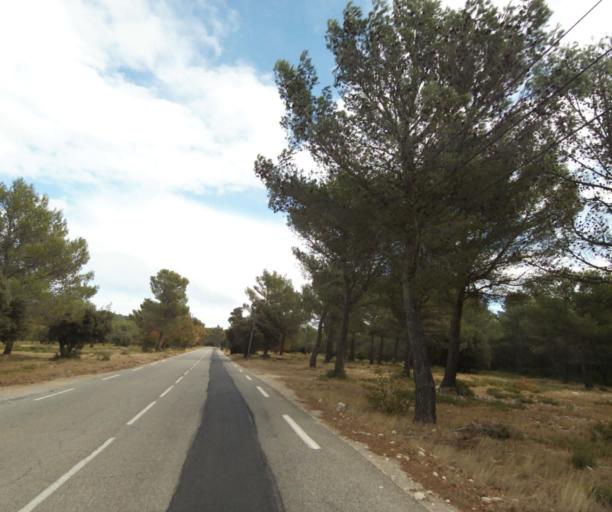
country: FR
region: Provence-Alpes-Cote d'Azur
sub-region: Departement des Bouches-du-Rhone
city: Cuges-les-Pins
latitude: 43.2411
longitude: 5.6985
